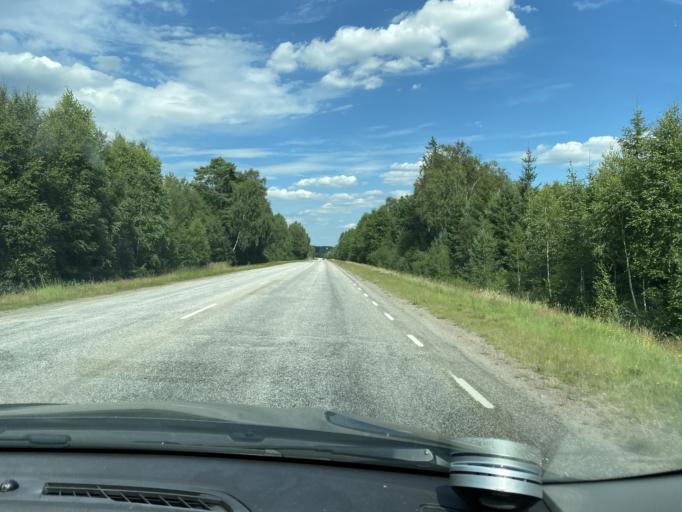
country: SE
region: Kronoberg
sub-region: Markaryds Kommun
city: Markaryd
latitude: 56.4360
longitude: 13.5764
